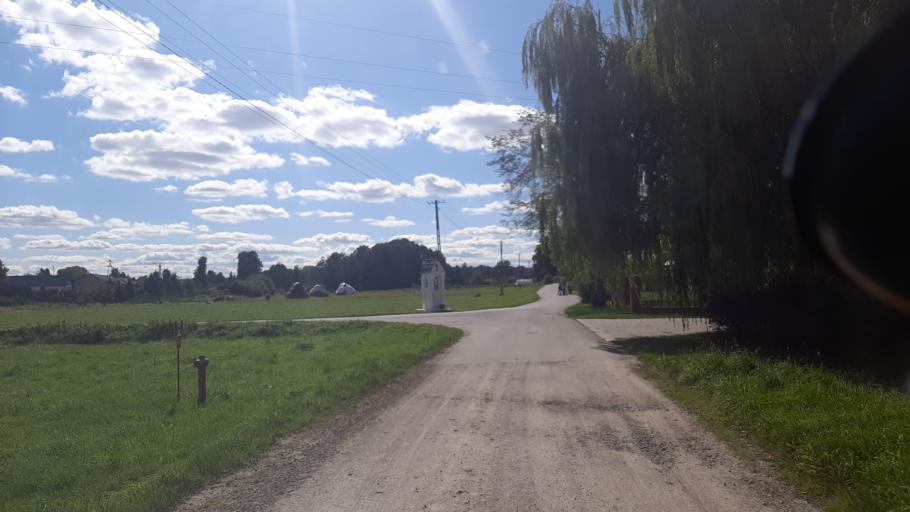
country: PL
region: Lublin Voivodeship
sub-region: Powiat lubartowski
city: Kamionka
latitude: 51.4061
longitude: 22.4146
